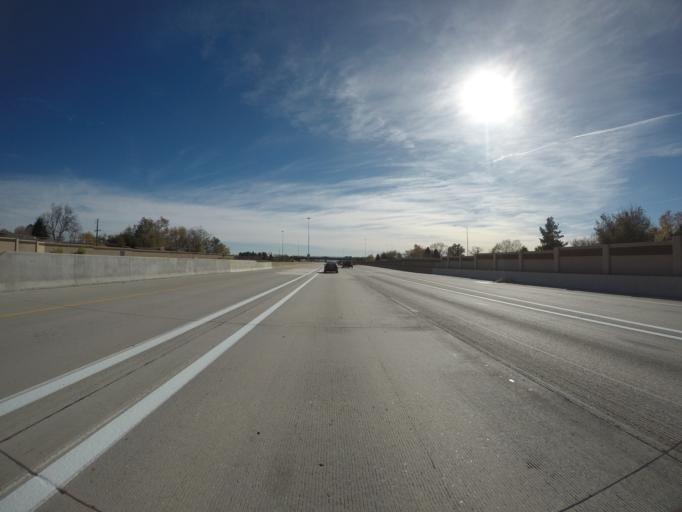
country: US
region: Colorado
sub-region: Adams County
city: Westminster
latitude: 39.8376
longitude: -105.0305
